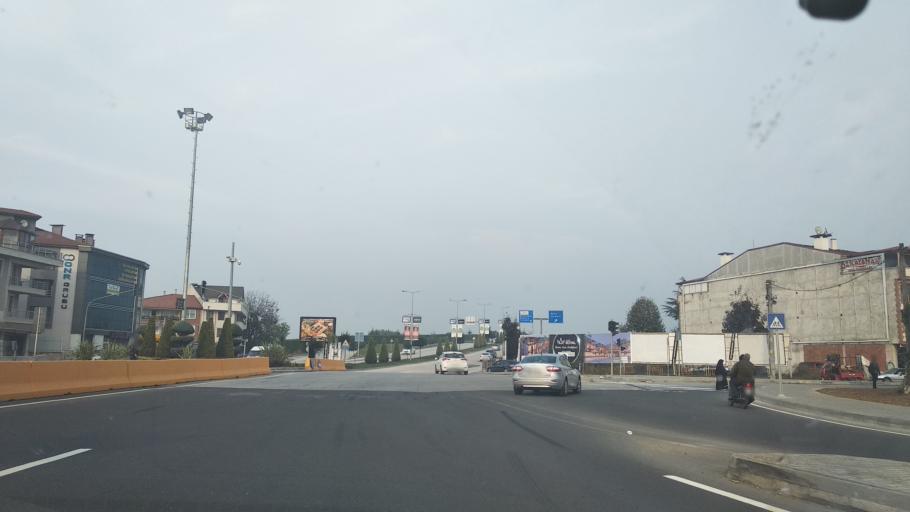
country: TR
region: Duzce
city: Duzce
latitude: 40.8356
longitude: 31.1710
